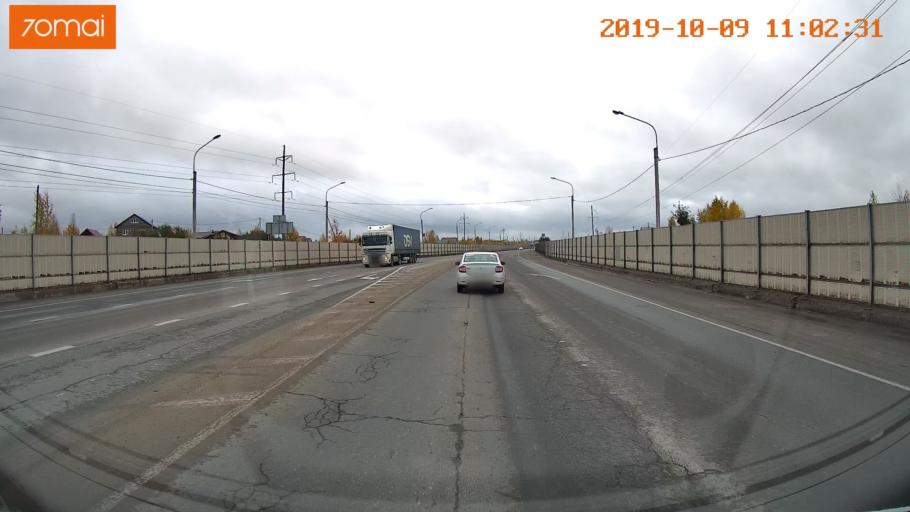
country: RU
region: Vologda
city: Vologda
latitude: 59.2316
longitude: 39.7743
